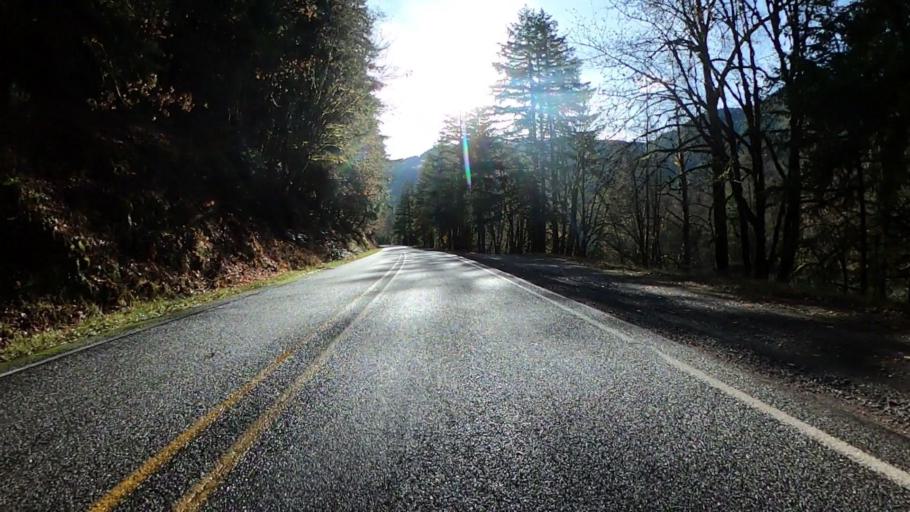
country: US
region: Oregon
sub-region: Lane County
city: Oakridge
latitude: 43.7529
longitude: -122.5264
